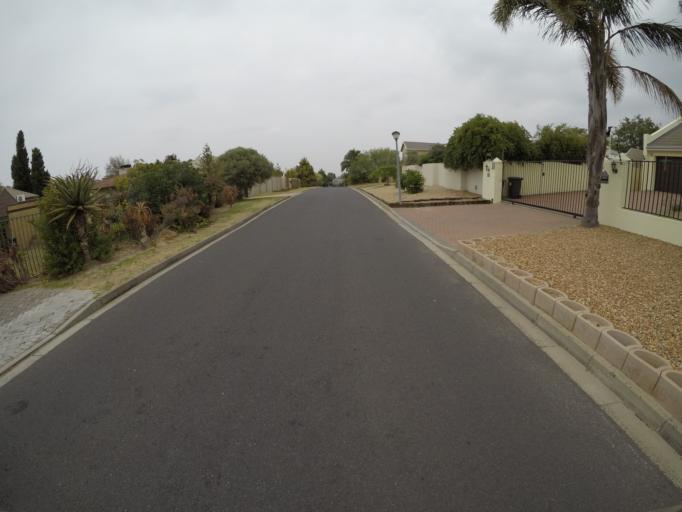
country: ZA
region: Western Cape
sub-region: City of Cape Town
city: Kraaifontein
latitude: -33.8691
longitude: 18.6449
